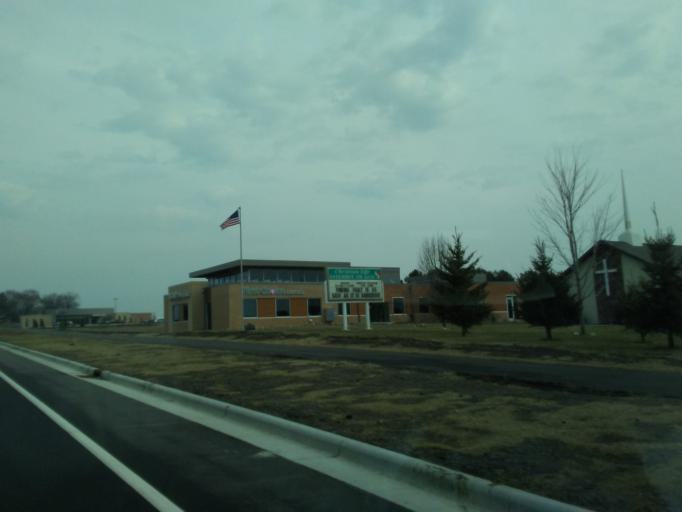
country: US
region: Wisconsin
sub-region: Dane County
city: Waunakee
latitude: 43.1705
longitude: -89.4618
